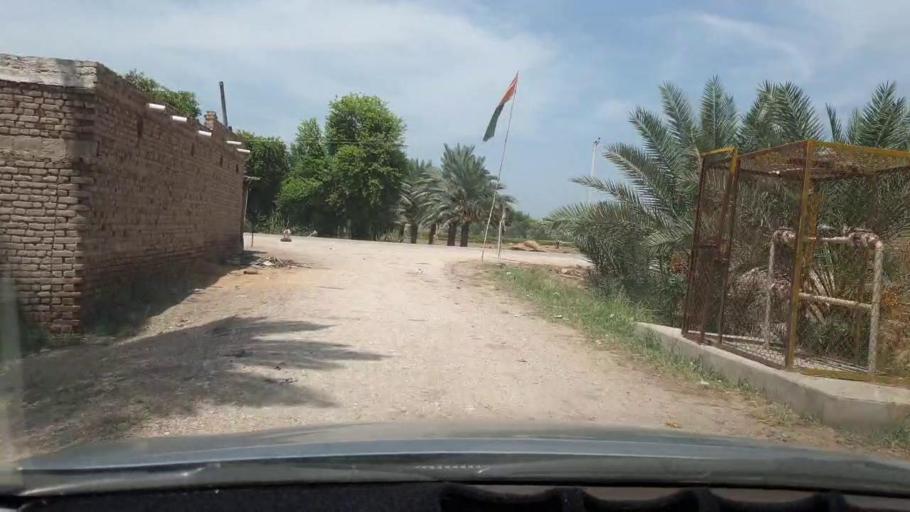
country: PK
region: Sindh
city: Khairpur
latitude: 27.4752
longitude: 68.7568
